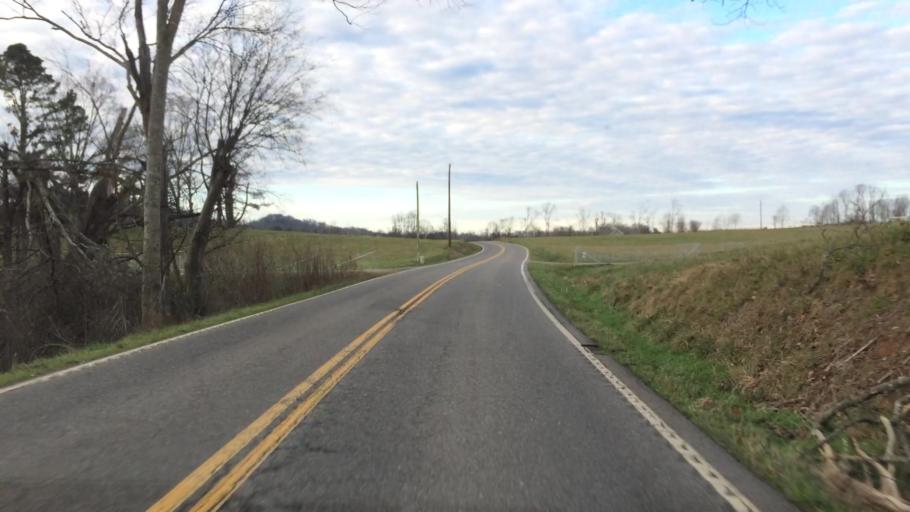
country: US
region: Tennessee
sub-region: McMinn County
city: Englewood
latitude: 35.4790
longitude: -84.5287
